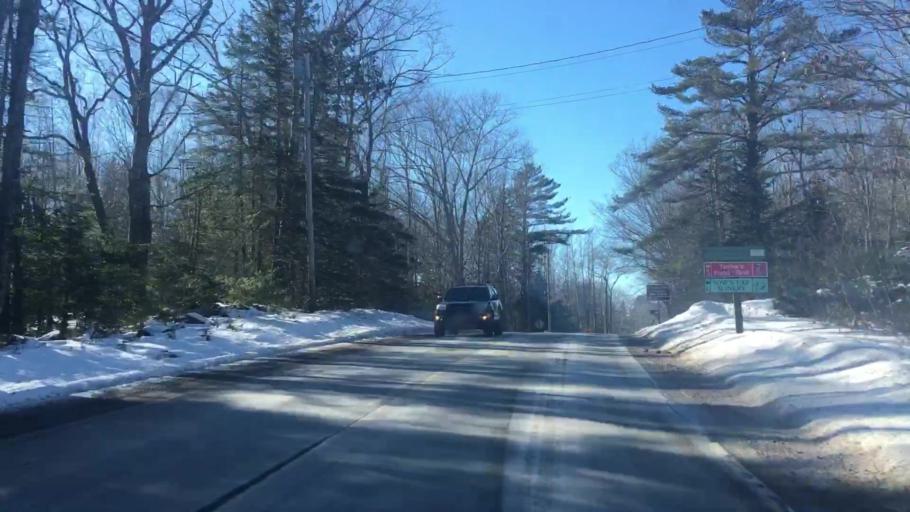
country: US
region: Maine
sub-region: Hancock County
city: Sedgwick
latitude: 44.3805
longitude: -68.6572
